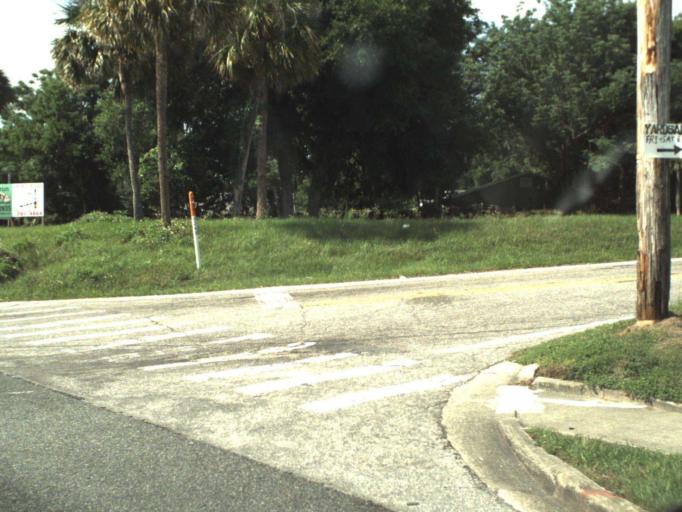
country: US
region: Florida
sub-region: Marion County
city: Ocala
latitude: 29.1646
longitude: -82.1353
